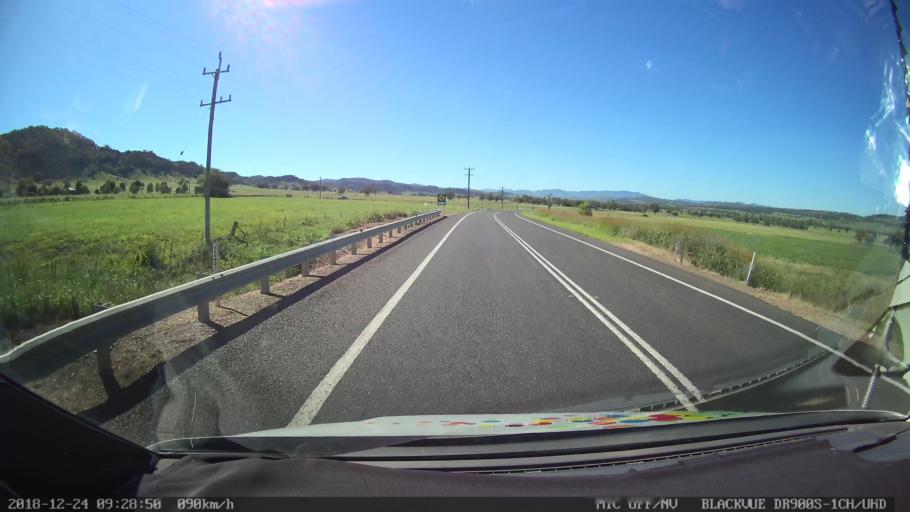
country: AU
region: New South Wales
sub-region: Liverpool Plains
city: Quirindi
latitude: -31.5424
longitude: 150.6917
